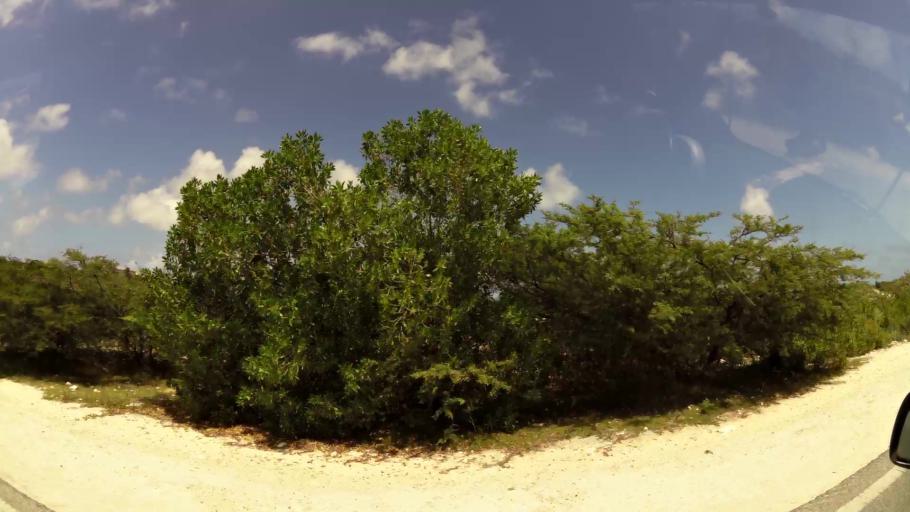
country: TC
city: Cockburn Town
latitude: 21.4303
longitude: -71.1444
